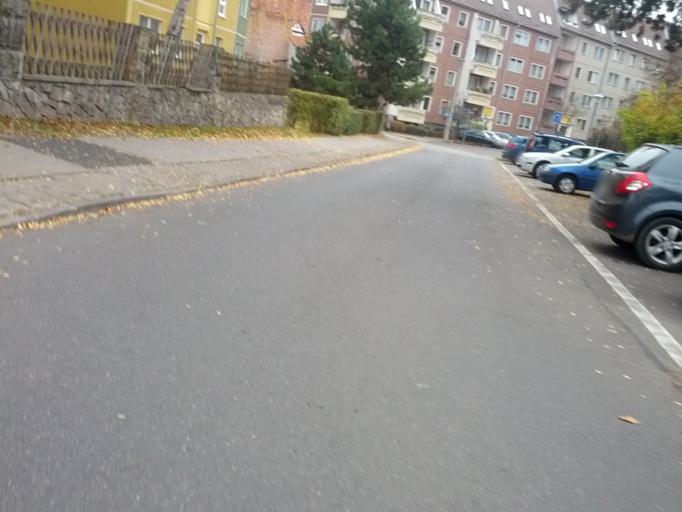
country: DE
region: Thuringia
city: Gotha
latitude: 50.9460
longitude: 10.6995
